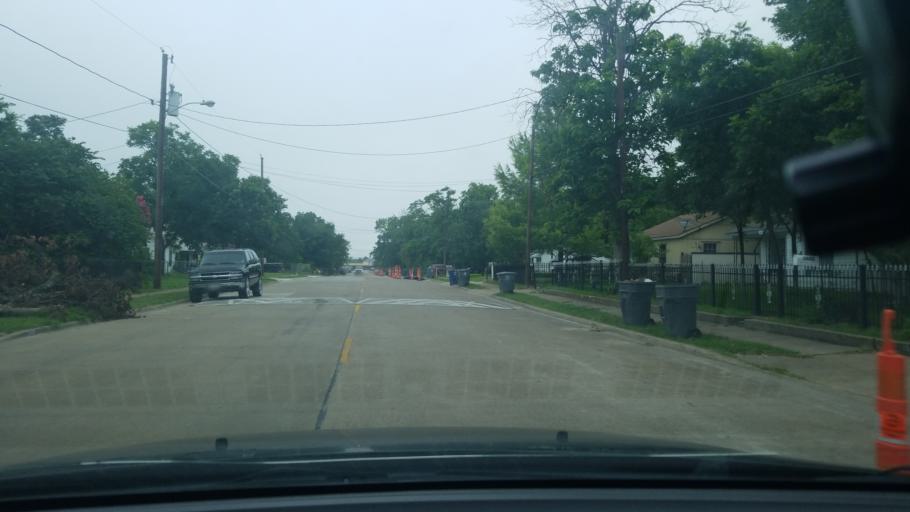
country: US
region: Texas
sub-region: Dallas County
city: Balch Springs
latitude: 32.7596
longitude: -96.6781
